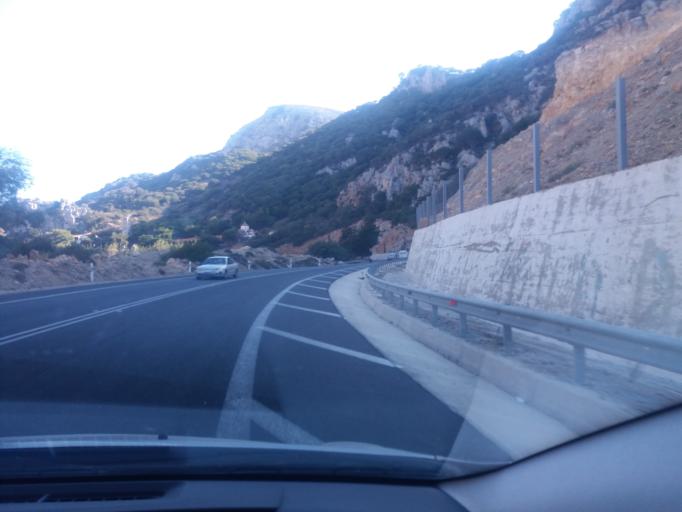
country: GR
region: Crete
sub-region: Nomos Lasithiou
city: Sision
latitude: 35.2876
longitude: 25.5382
